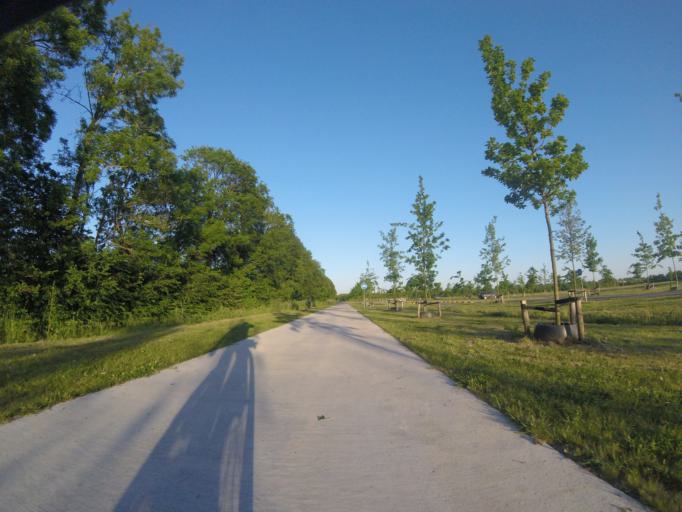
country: NL
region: North Holland
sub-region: Gemeente Haarlemmermeer
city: Hoofddorp
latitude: 52.3711
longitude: 4.7513
